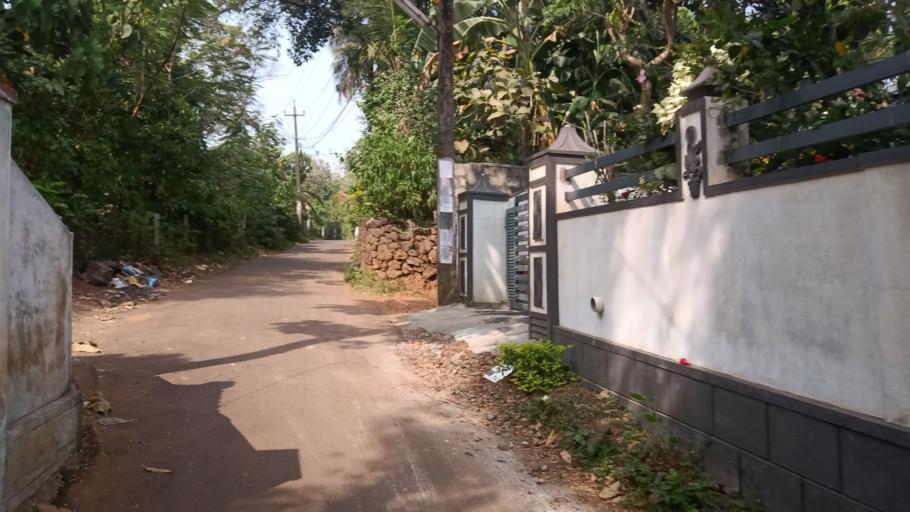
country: IN
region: Kerala
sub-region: Palakkad district
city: Cherpulassery
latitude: 10.8851
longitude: 76.3150
